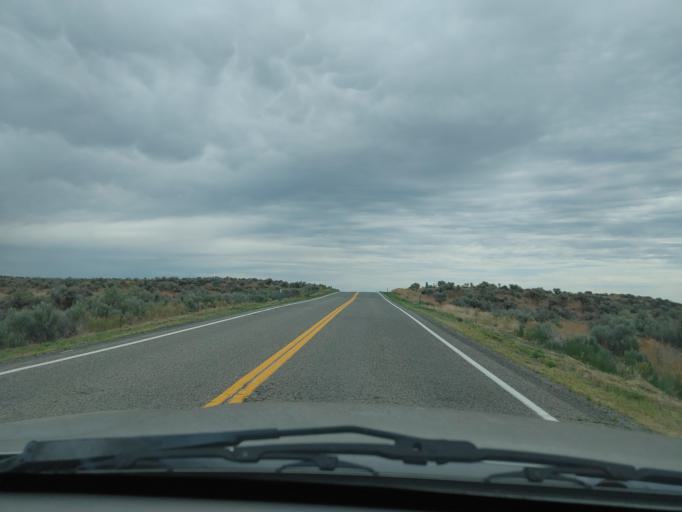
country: US
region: Idaho
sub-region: Lincoln County
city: Shoshone
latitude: 43.0726
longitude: -114.1091
